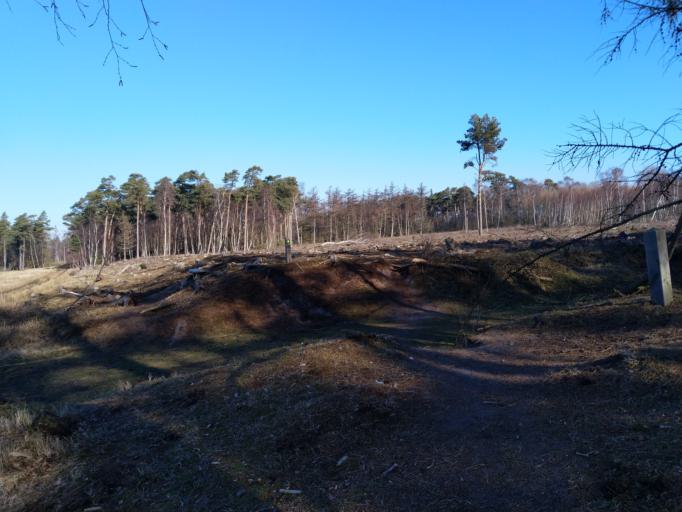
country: DK
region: Zealand
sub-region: Guldborgsund Kommune
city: Nykobing Falster
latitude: 54.6406
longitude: 11.9574
